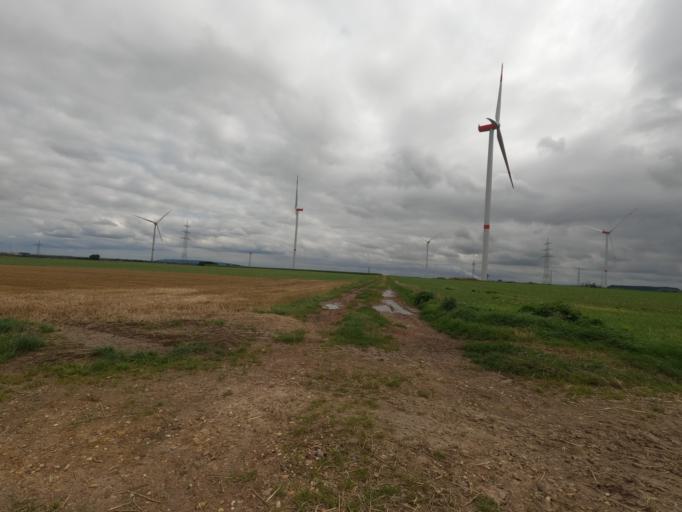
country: DE
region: North Rhine-Westphalia
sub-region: Regierungsbezirk Koln
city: Linnich
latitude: 50.9801
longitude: 6.2231
